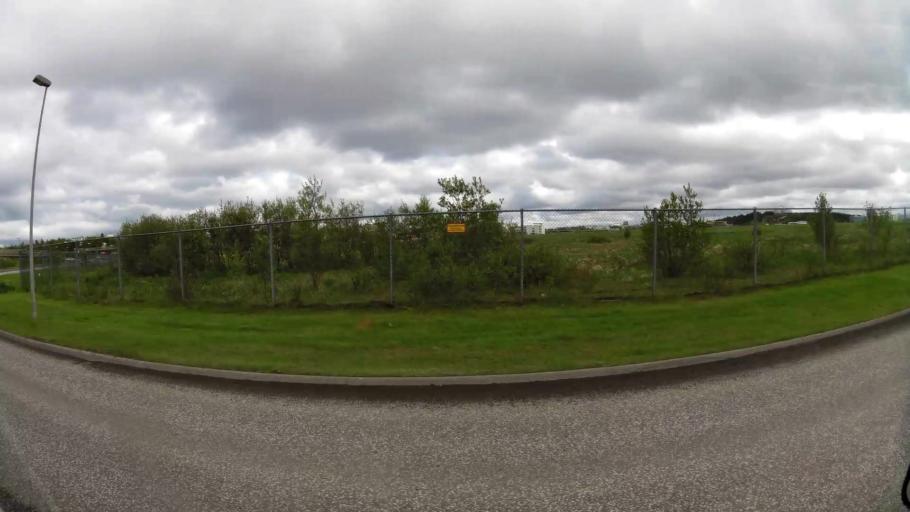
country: IS
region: Capital Region
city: Kopavogur
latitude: 64.1369
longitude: -21.9430
